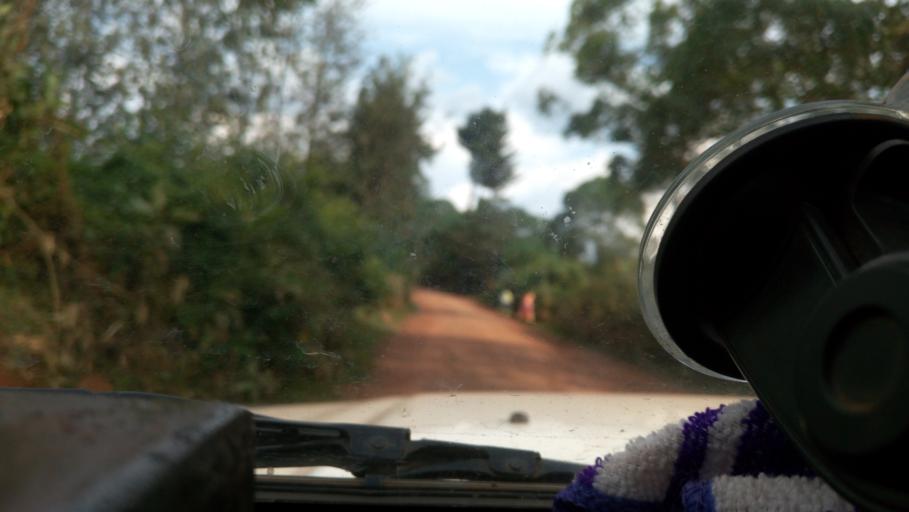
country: KE
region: Kericho
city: Litein
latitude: -0.4470
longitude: 35.1014
